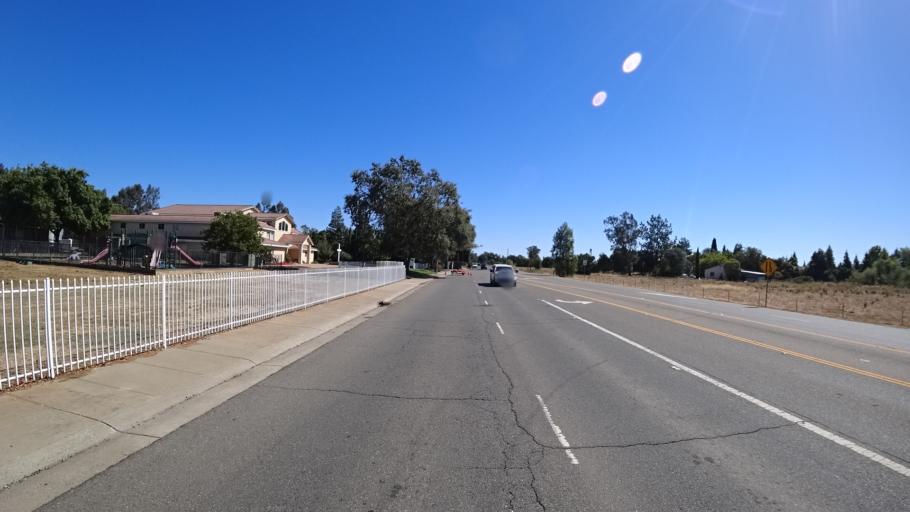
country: US
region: California
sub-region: Sacramento County
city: Elk Grove
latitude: 38.4237
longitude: -121.3341
